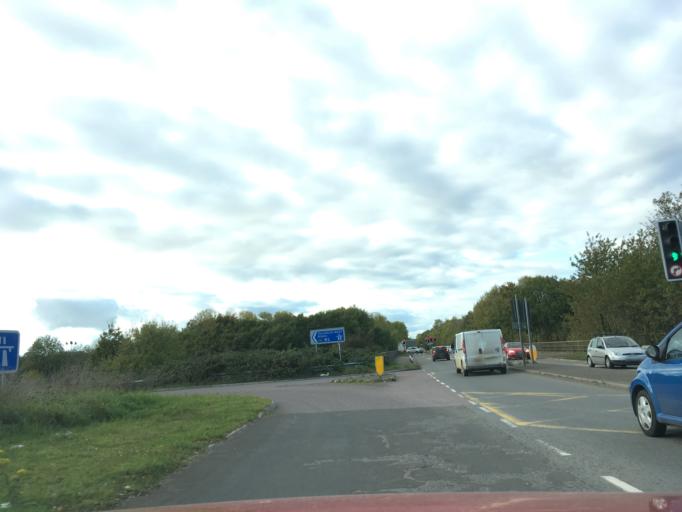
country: GB
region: England
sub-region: South Gloucestershire
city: Falfield
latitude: 51.6363
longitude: -2.4512
